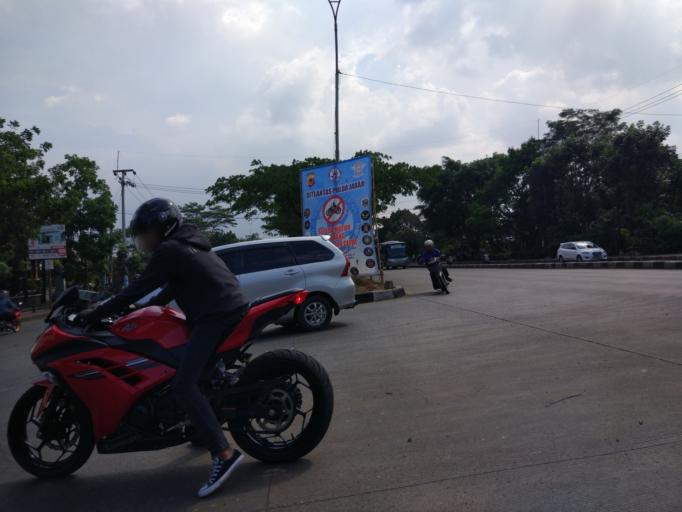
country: ID
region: West Java
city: Cileunyi
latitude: -6.9355
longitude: 107.7135
